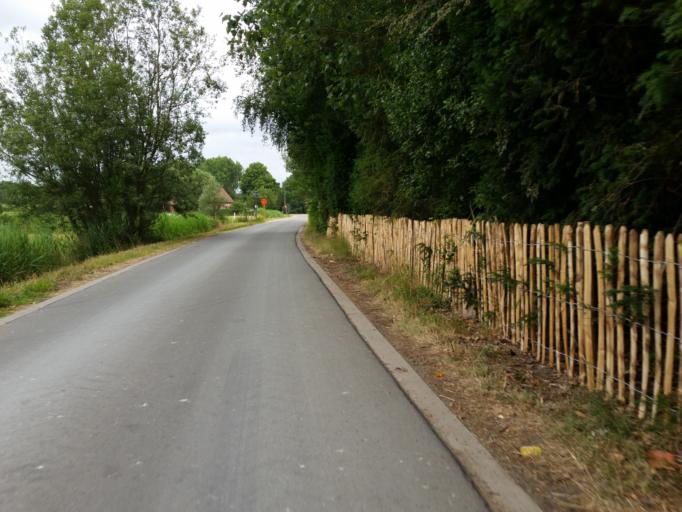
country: BE
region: Flanders
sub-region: Provincie Antwerpen
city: Rumst
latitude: 51.0698
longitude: 4.4390
